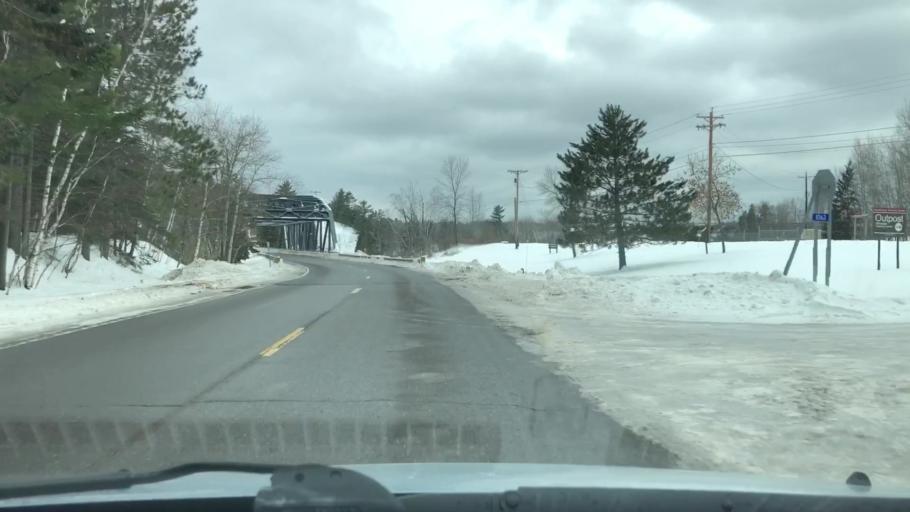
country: US
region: Minnesota
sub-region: Carlton County
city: Carlton
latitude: 46.6648
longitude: -92.4027
